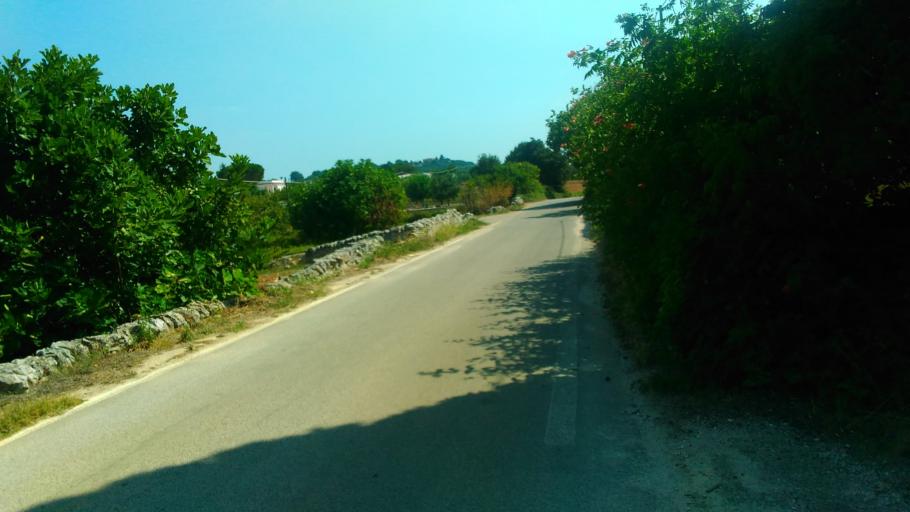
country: IT
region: Apulia
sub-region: Provincia di Bari
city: Locorotondo
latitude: 40.7512
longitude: 17.3590
